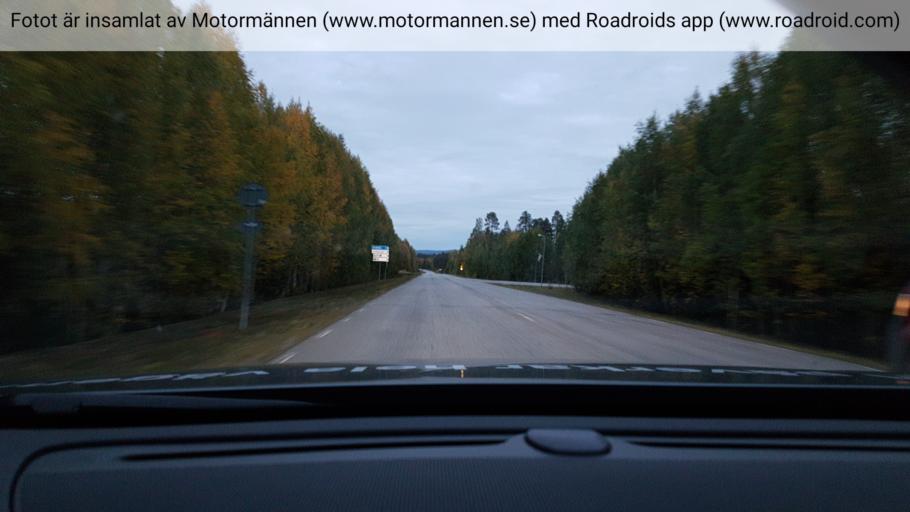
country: SE
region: Norrbotten
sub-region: Alvsbyns Kommun
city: AElvsbyn
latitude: 65.8406
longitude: 20.5014
